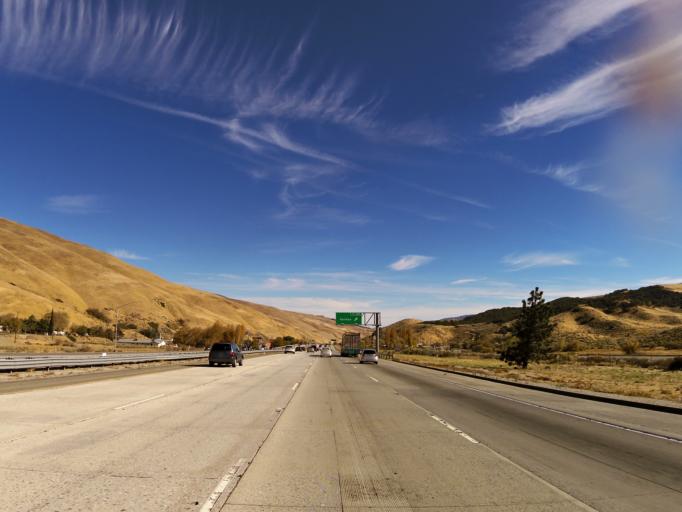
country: US
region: California
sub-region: Kern County
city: Lebec
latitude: 34.7958
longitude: -118.8609
